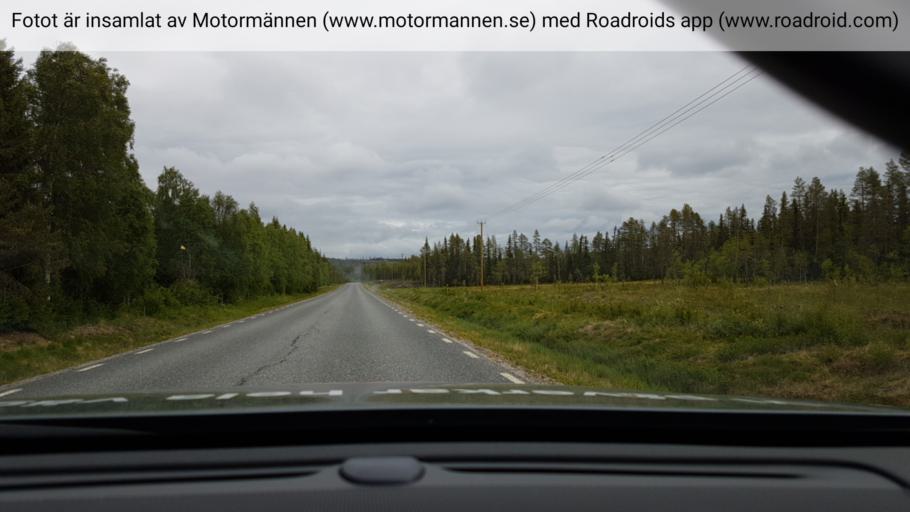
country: SE
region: Vaesterbotten
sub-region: Asele Kommun
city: Insjon
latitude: 64.3119
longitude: 17.6966
